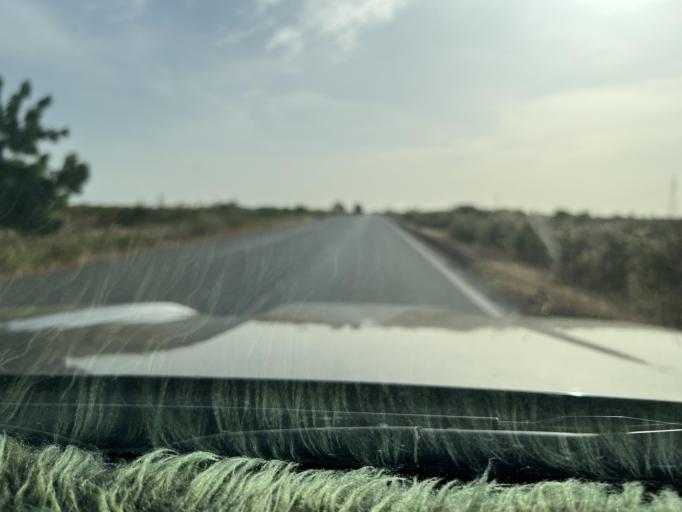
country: ML
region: Segou
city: Baroueli
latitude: 12.9544
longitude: -6.7282
